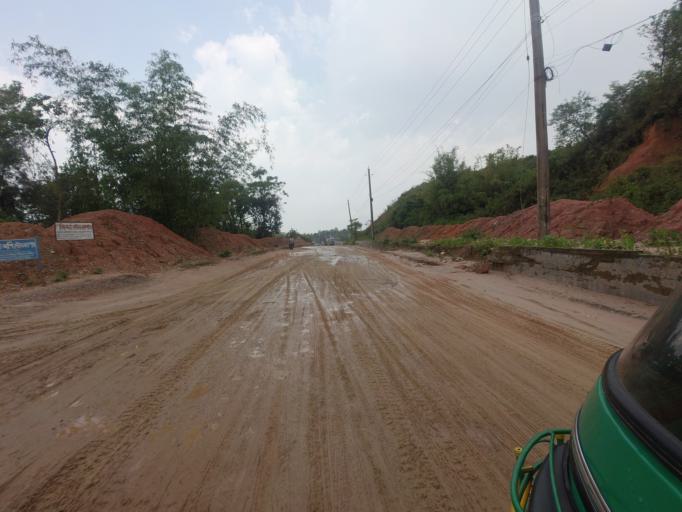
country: BD
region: Sylhet
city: Sylhet
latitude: 24.9649
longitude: 91.8768
